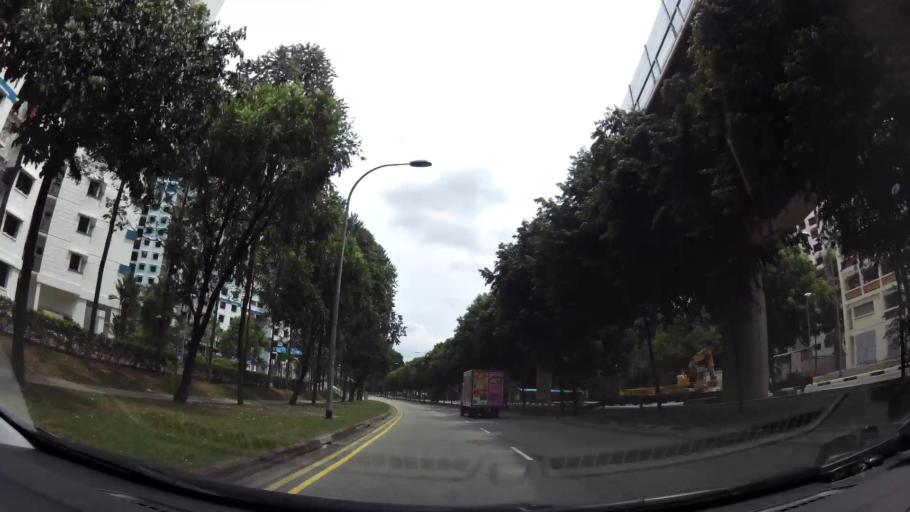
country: MY
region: Johor
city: Johor Bahru
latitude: 1.3378
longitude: 103.7023
